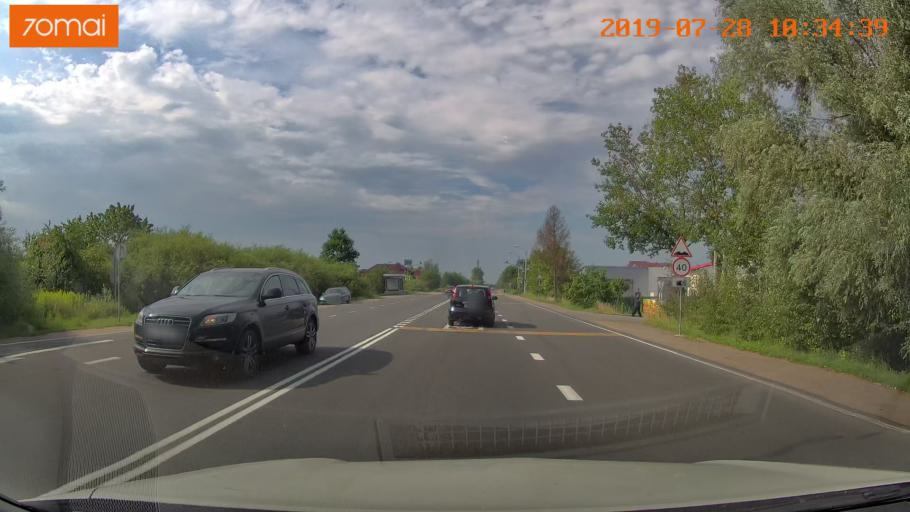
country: RU
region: Kaliningrad
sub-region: Gorod Kaliningrad
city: Kaliningrad
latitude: 54.7519
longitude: 20.4376
